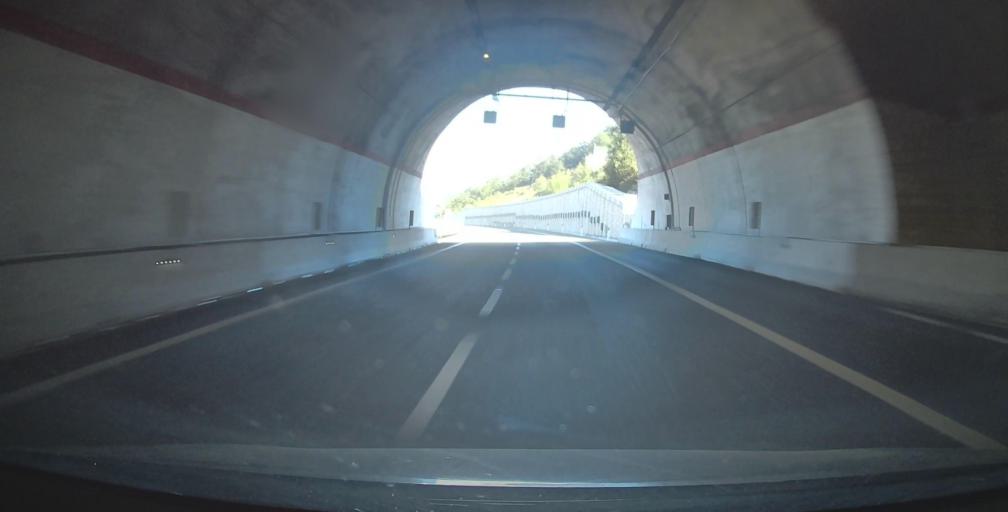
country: IT
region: Basilicate
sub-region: Provincia di Potenza
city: Lauria
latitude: 40.0708
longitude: 15.8677
